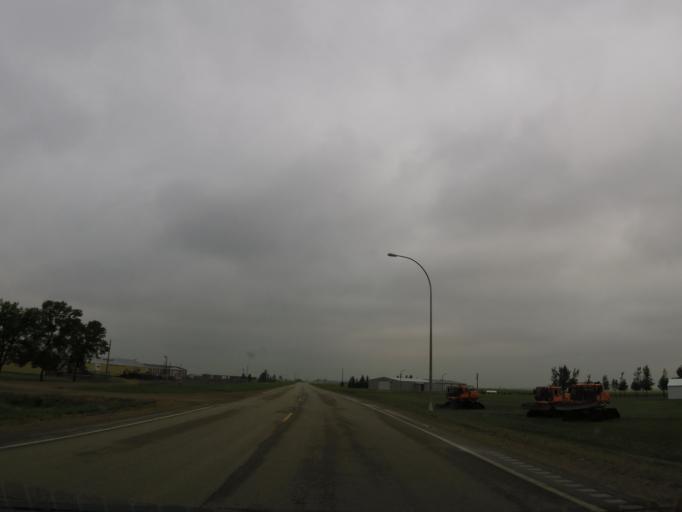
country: US
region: Minnesota
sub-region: Marshall County
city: Warren
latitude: 48.2040
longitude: -96.7731
